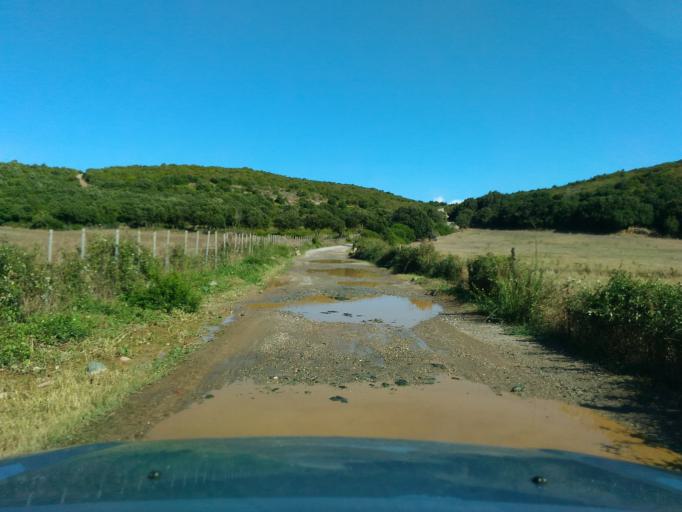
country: FR
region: Corsica
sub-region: Departement de la Haute-Corse
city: Brando
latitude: 42.9688
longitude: 9.4518
